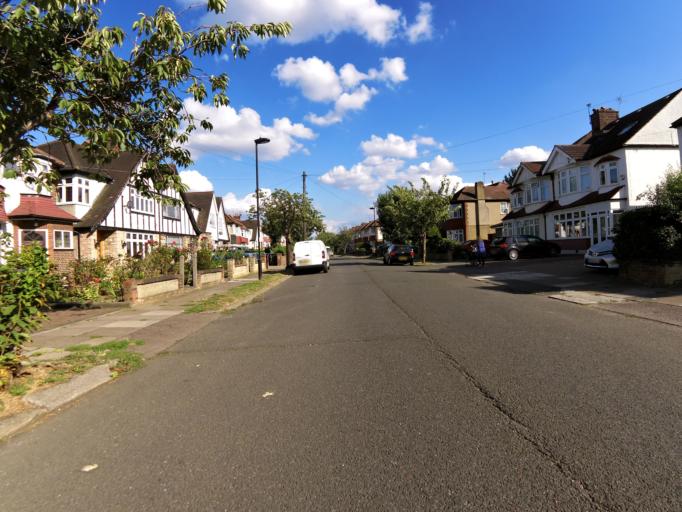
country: GB
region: England
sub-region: Greater London
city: Wood Green
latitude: 51.6160
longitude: -0.1234
